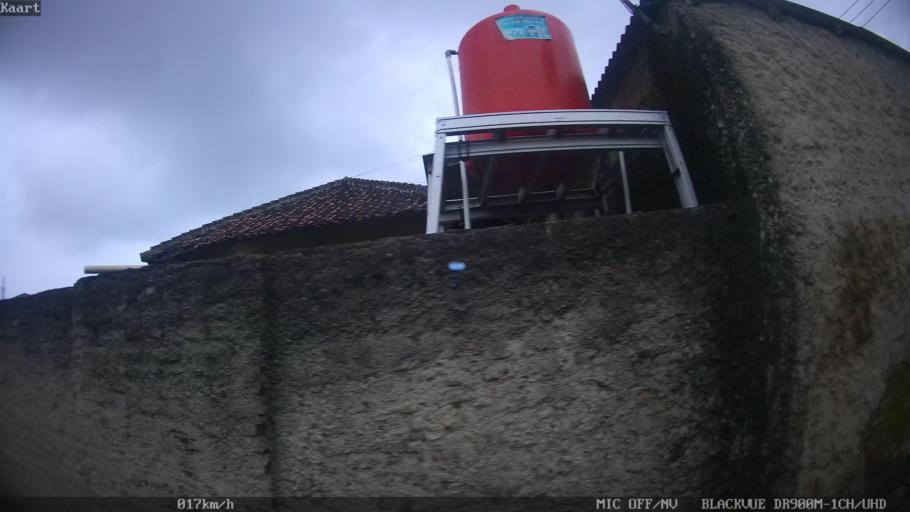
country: ID
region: Lampung
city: Bandarlampung
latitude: -5.4114
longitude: 105.2788
